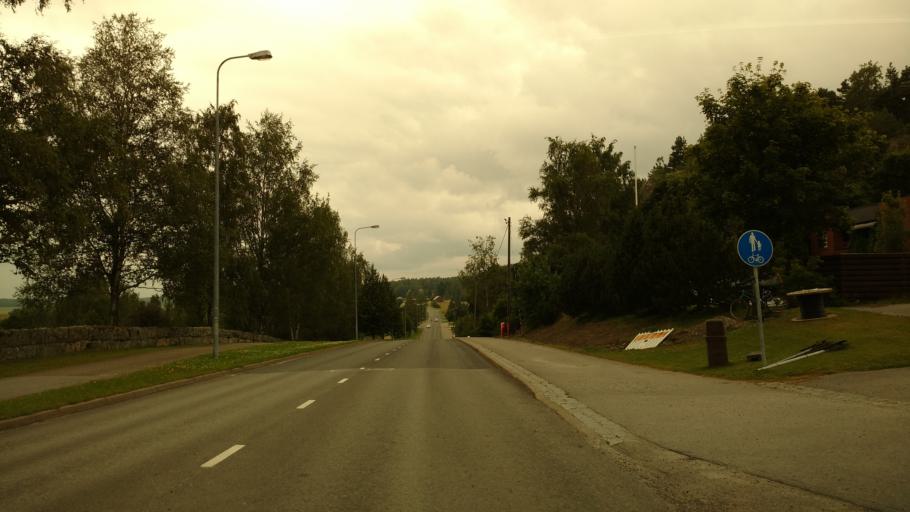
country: FI
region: Varsinais-Suomi
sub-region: Salo
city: Halikko
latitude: 60.4008
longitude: 23.0735
